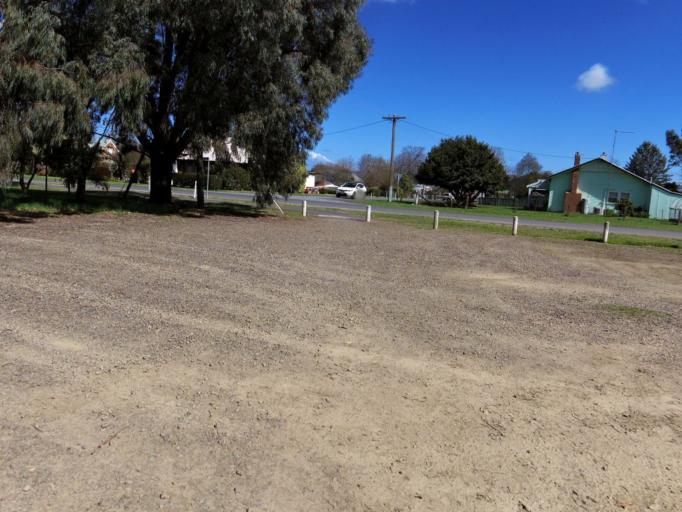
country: AU
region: Victoria
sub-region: Murrindindi
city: Alexandra
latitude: -37.1845
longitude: 145.7137
